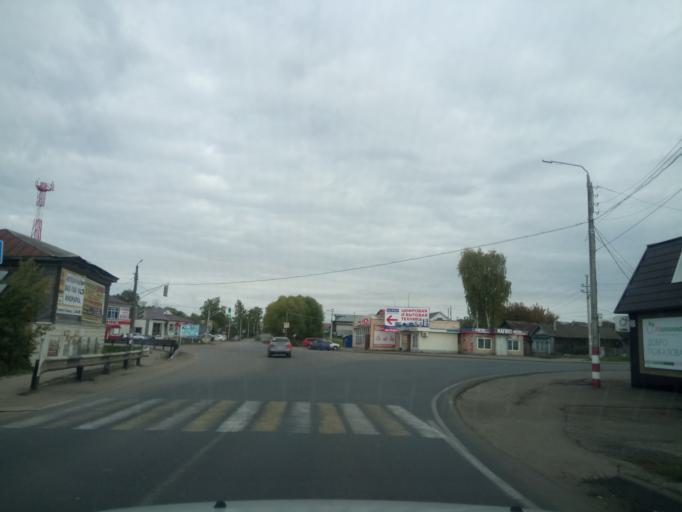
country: RU
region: Nizjnij Novgorod
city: Lukoyanov
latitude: 55.0296
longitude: 44.4913
